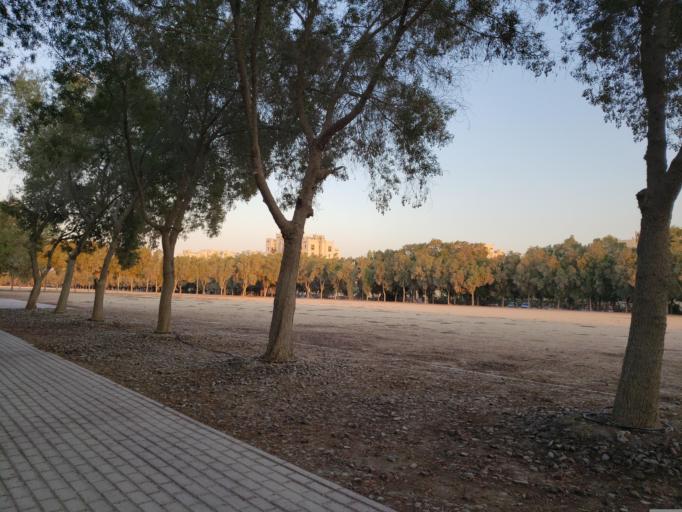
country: AE
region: Dubai
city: Dubai
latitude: 25.0073
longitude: 55.2469
